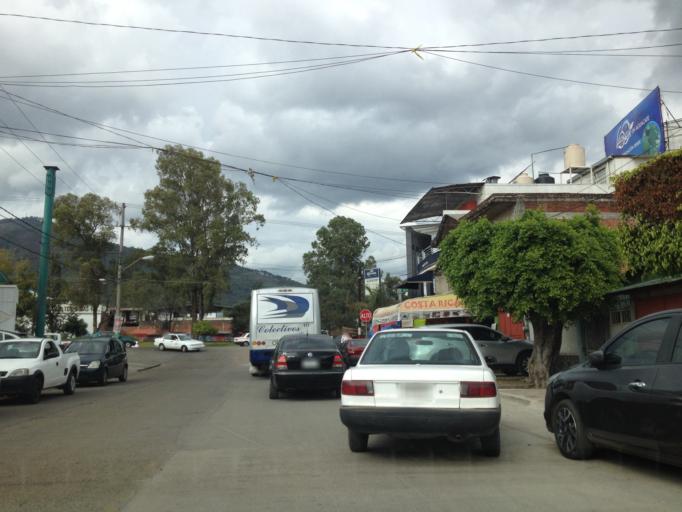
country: MX
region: Michoacan
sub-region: Uruapan
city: Uruapan
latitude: 19.4214
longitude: -102.0364
